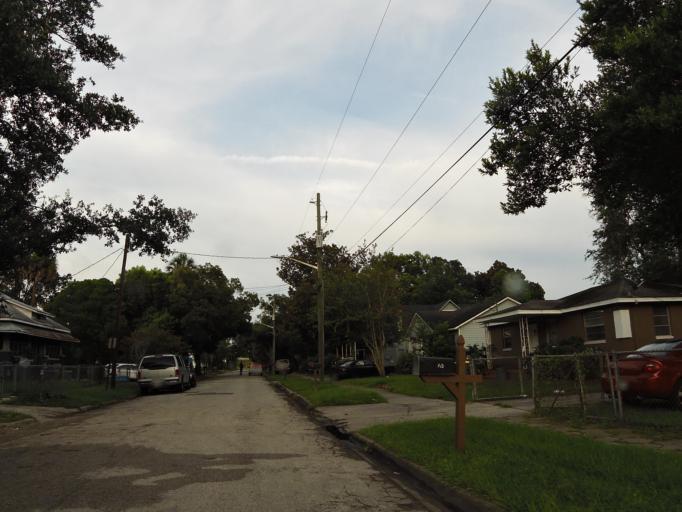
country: US
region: Florida
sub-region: Duval County
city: Jacksonville
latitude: 30.3529
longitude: -81.6401
